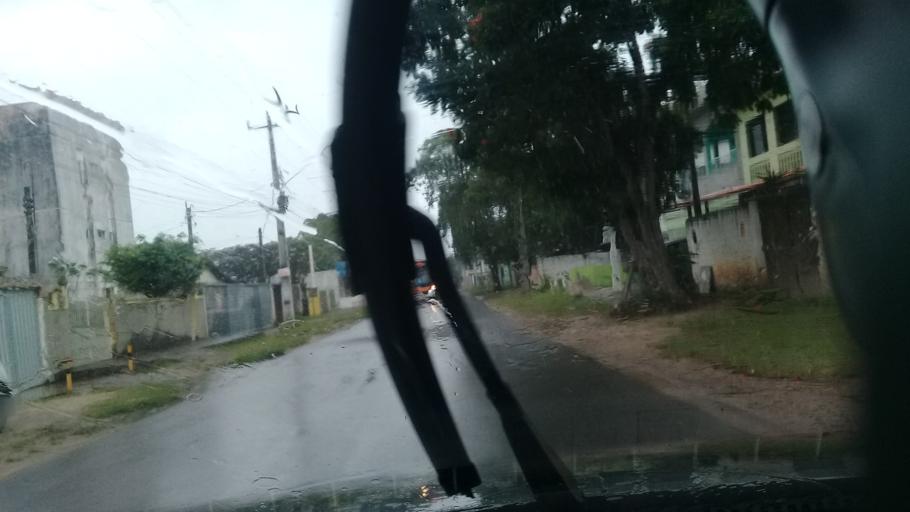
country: BR
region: Pernambuco
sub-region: Itamaraca
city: Itamaraca
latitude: -7.7401
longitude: -34.8248
